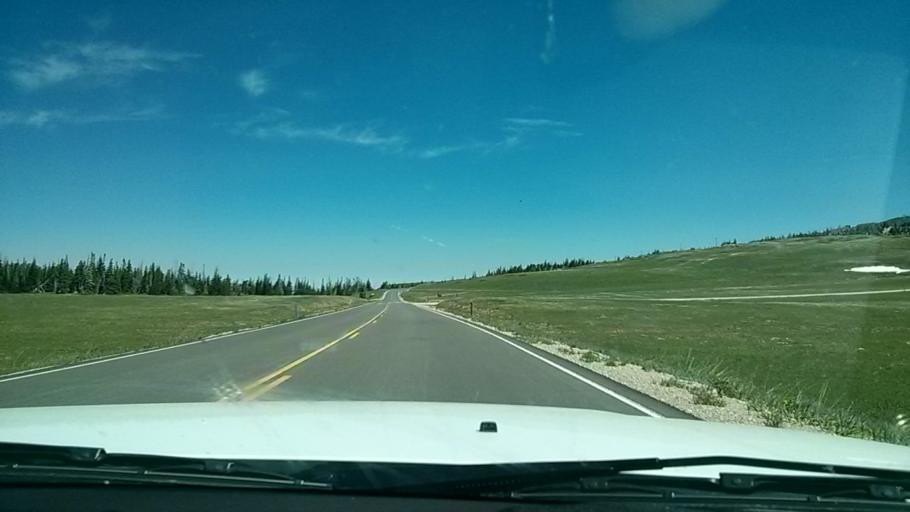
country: US
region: Utah
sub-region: Iron County
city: Parowan
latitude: 37.6666
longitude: -112.8386
